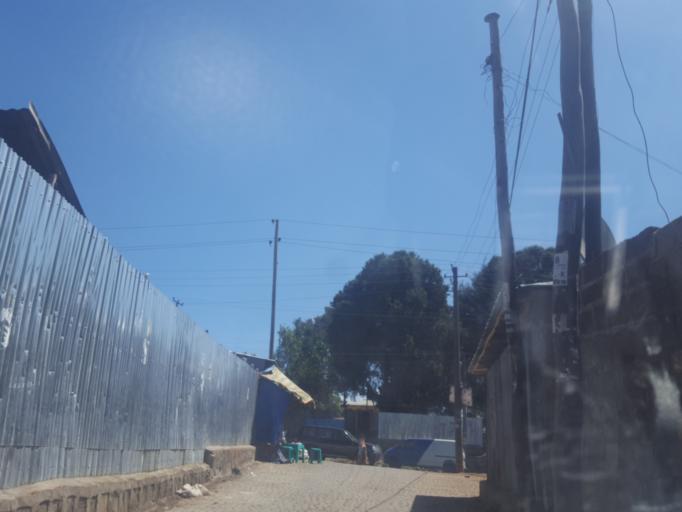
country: ET
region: Adis Abeba
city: Addis Ababa
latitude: 9.0673
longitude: 38.7337
